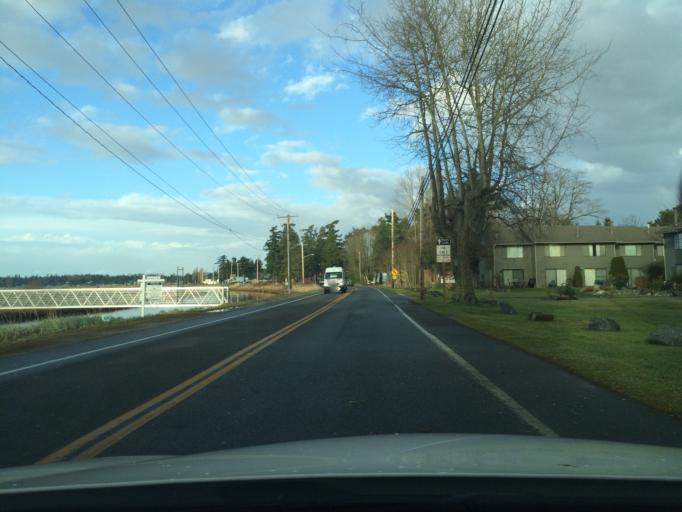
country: US
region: Washington
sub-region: Whatcom County
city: Birch Bay
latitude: 48.9188
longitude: -122.7449
